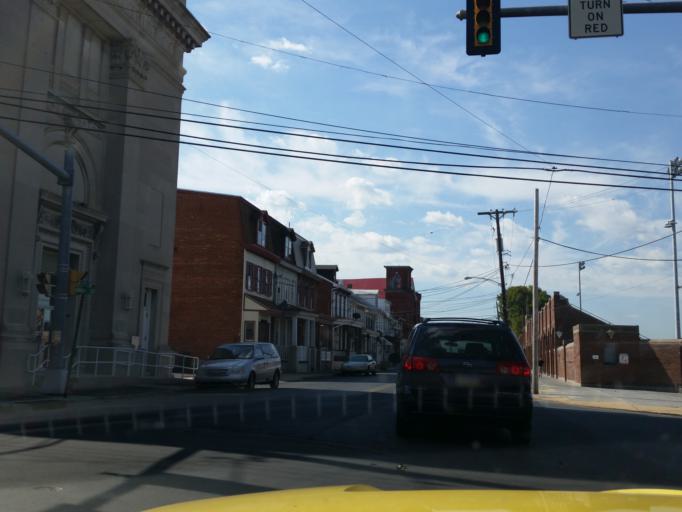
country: US
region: Pennsylvania
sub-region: Lebanon County
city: Lebanon
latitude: 40.3459
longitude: -76.4226
